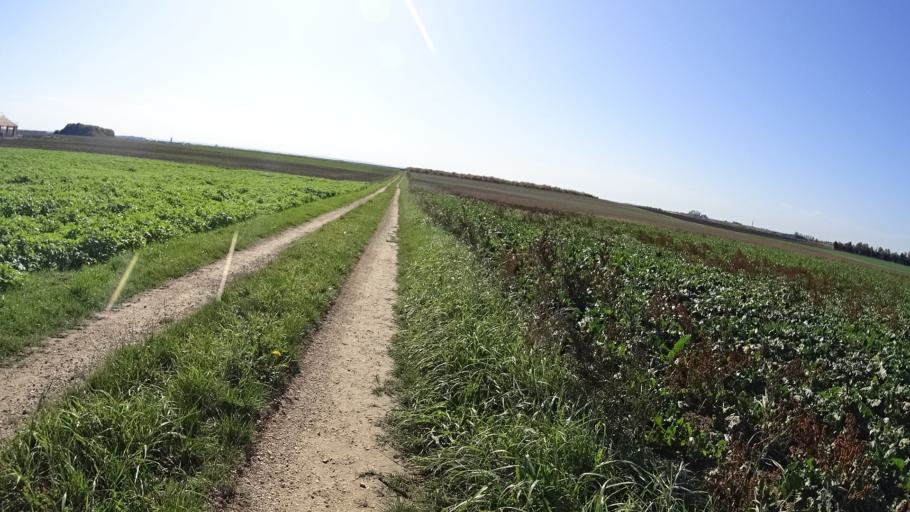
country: DE
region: Bavaria
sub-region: Upper Bavaria
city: Gaimersheim
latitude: 48.8315
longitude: 11.3510
